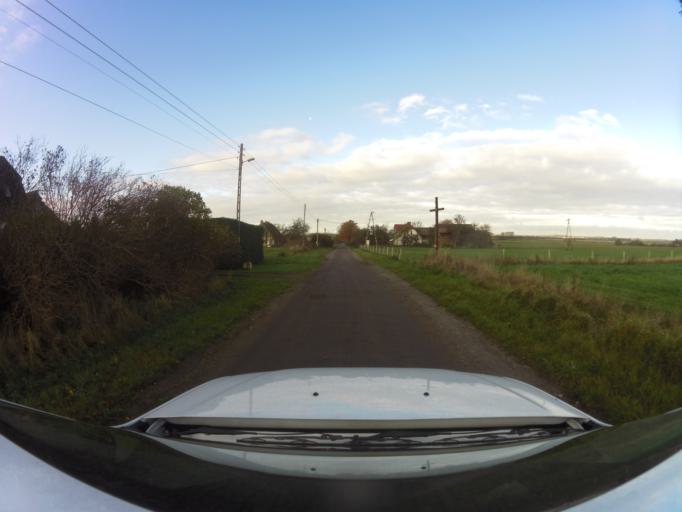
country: PL
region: West Pomeranian Voivodeship
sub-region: Powiat gryficki
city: Trzebiatow
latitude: 54.0488
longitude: 15.2051
